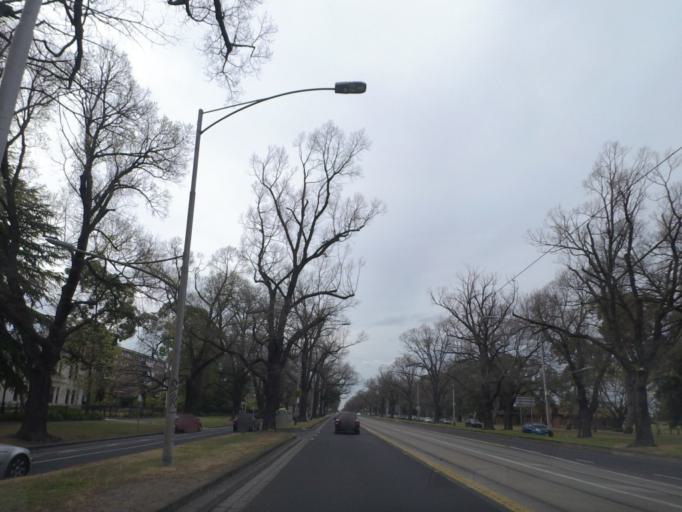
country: AU
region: Victoria
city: Carlton North
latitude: -37.7893
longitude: 144.9587
